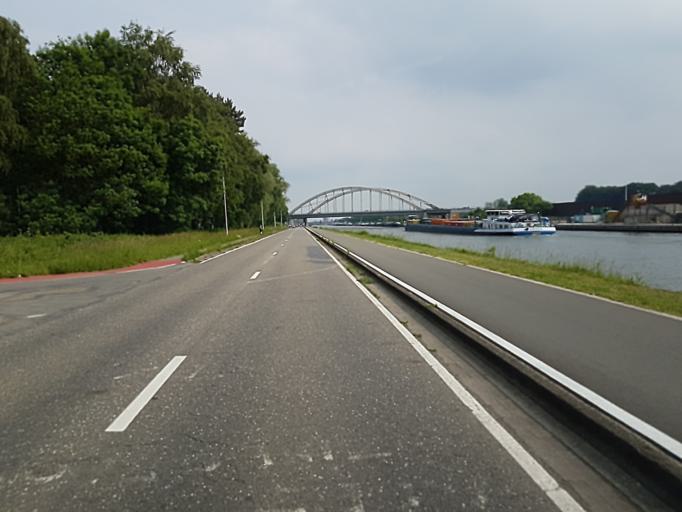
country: BE
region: Flanders
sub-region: Provincie Antwerpen
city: Wijnegem
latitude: 51.2361
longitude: 4.5105
